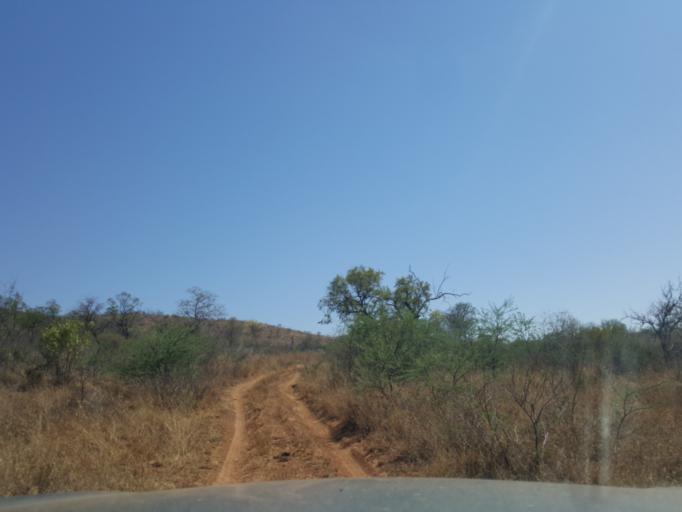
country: BW
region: South East
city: Lobatse
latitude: -25.1472
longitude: 25.6700
